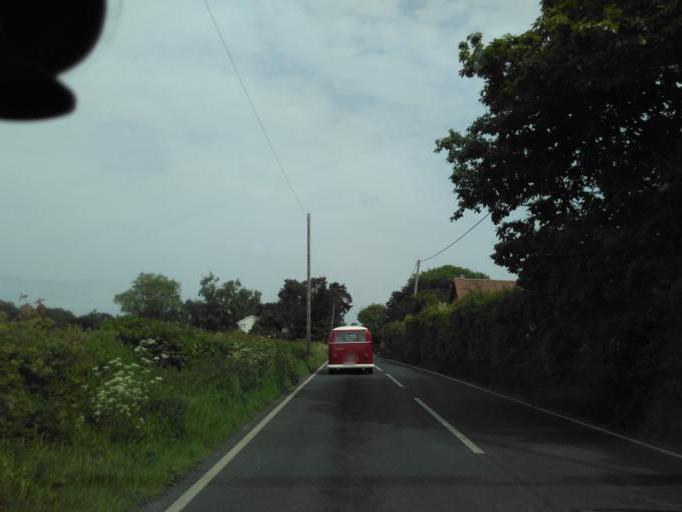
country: GB
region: England
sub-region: Kent
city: Chartham
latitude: 51.2130
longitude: 1.0598
